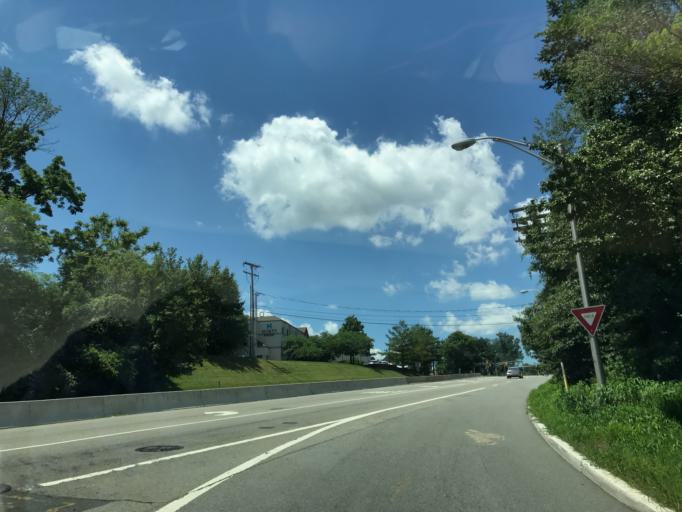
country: US
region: New Jersey
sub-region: Morris County
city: Madison
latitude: 40.7929
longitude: -74.4315
